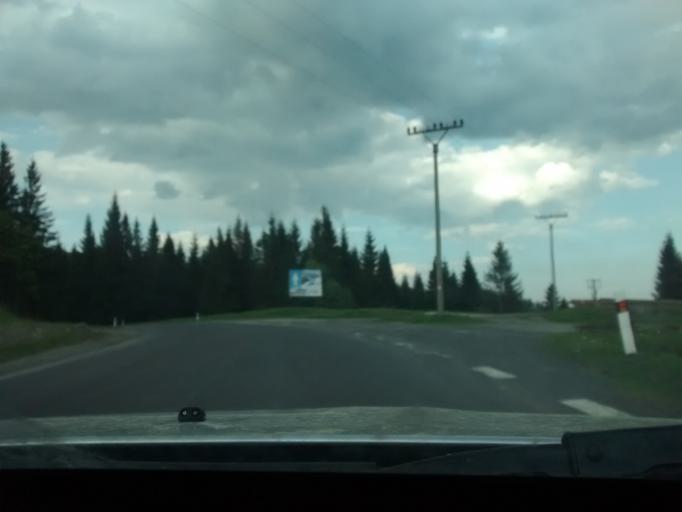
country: SK
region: Presovsky
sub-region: Okres Poprad
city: Zdiar
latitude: 49.2776
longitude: 20.2063
